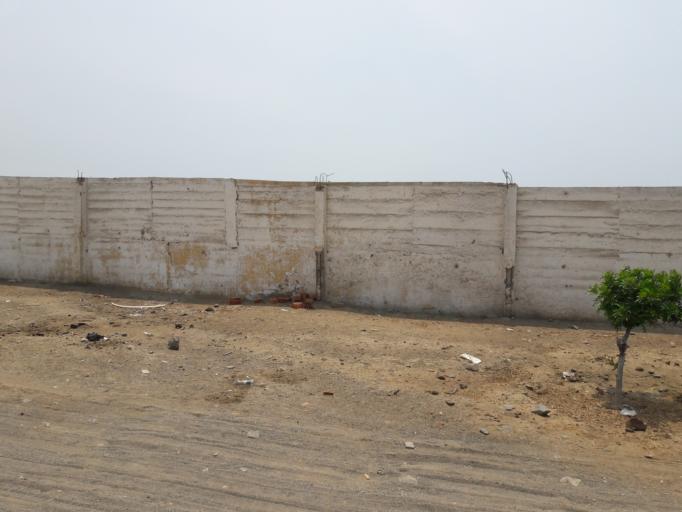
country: PE
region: Lima
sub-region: Lima
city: Santa Rosa
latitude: -11.7659
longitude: -77.1664
